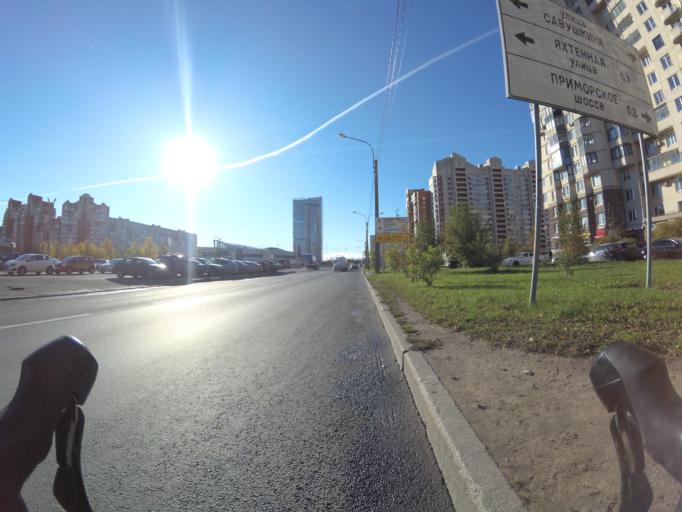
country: RU
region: Leningrad
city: Untolovo
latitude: 59.9898
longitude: 30.2033
